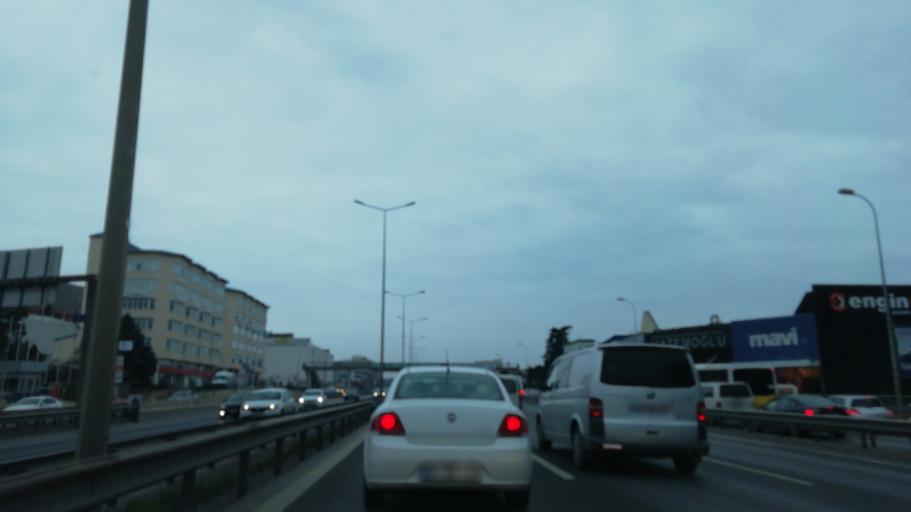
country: TR
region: Istanbul
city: Pendik
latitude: 40.8935
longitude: 29.2307
